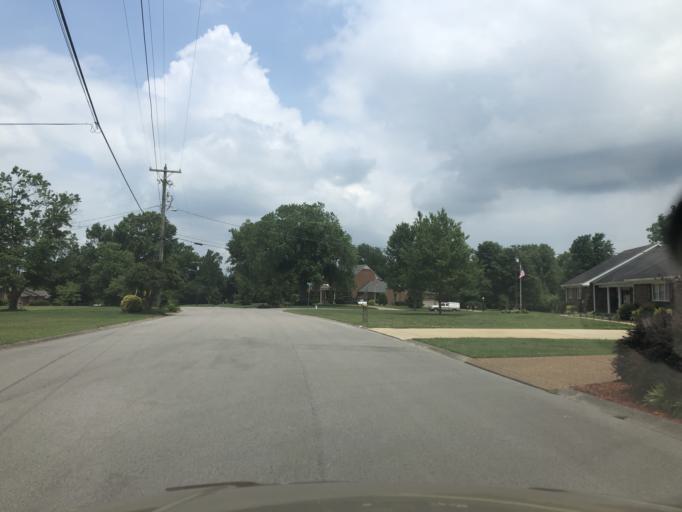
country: US
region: Tennessee
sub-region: Davidson County
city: Lakewood
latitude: 36.2388
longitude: -86.6149
